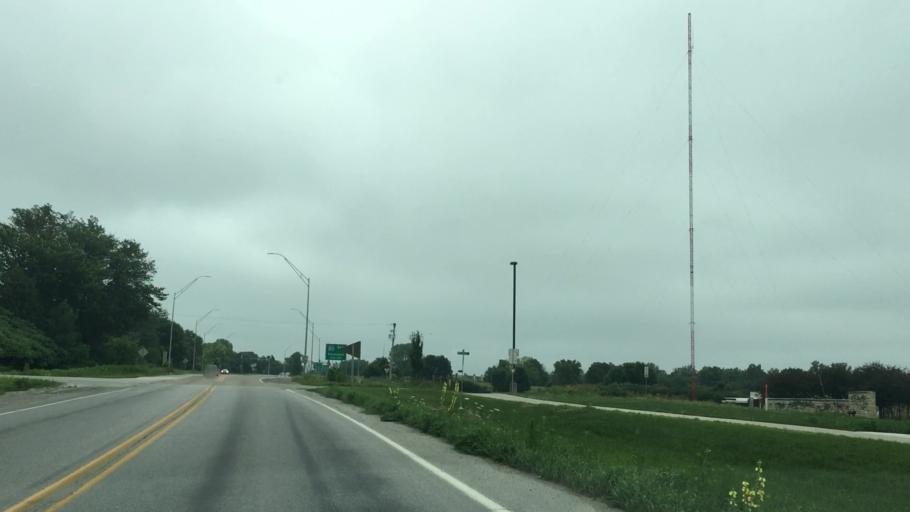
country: US
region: Iowa
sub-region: Johnson County
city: Iowa City
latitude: 41.6898
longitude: -91.5449
